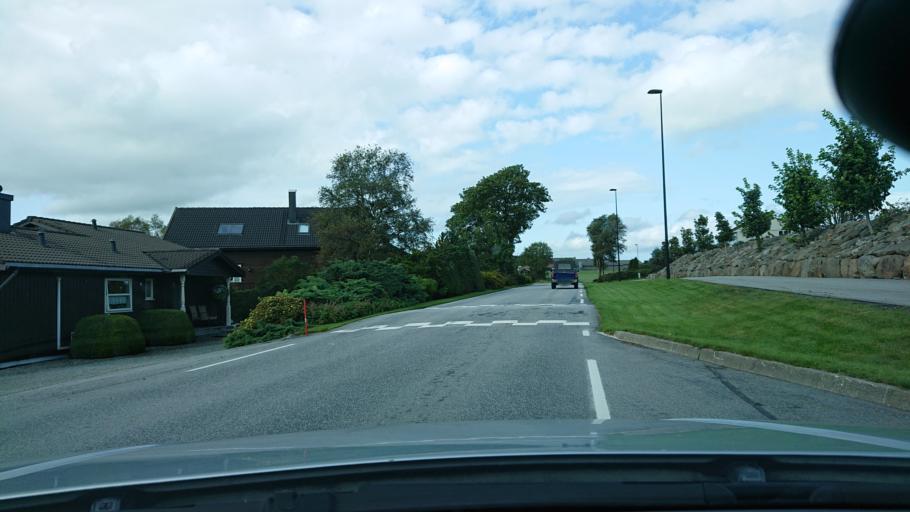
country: NO
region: Rogaland
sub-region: Gjesdal
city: Algard
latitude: 58.6872
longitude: 5.7678
